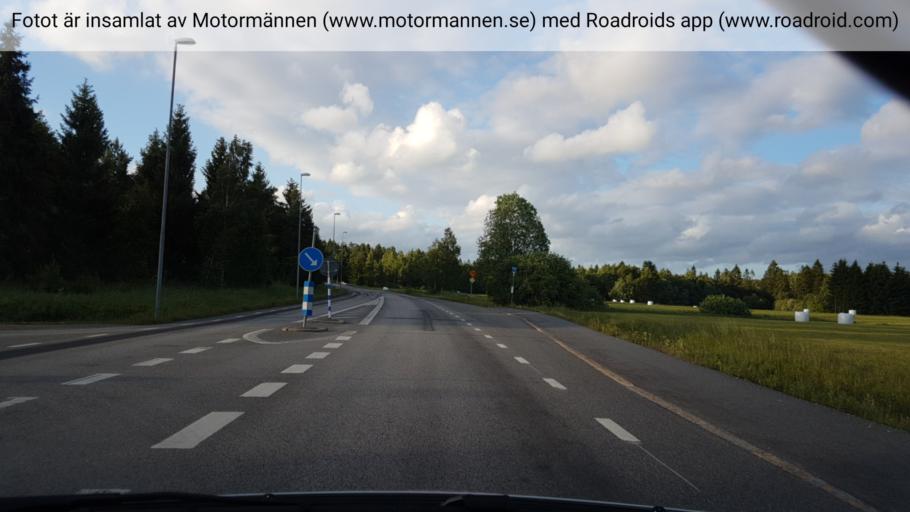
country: SE
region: OErebro
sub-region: Karlskoga Kommun
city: Karlskoga
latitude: 59.3425
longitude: 14.5797
